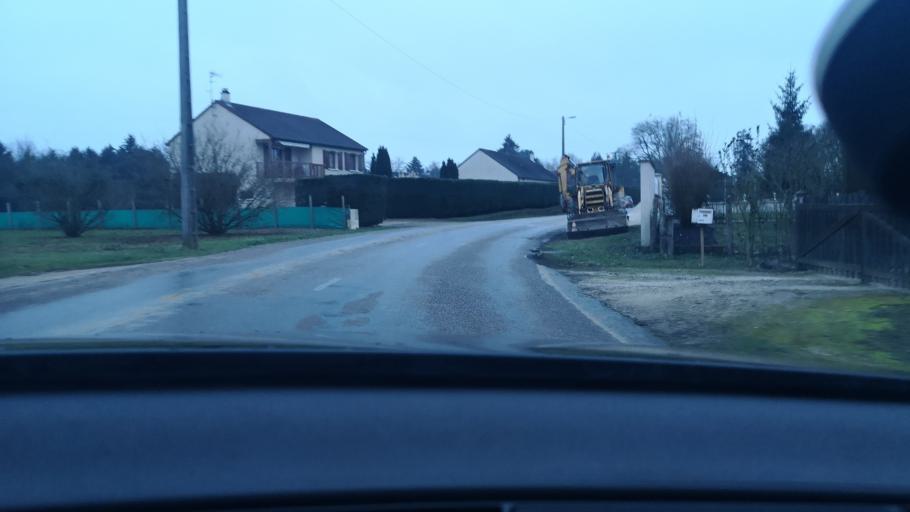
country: FR
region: Bourgogne
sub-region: Departement de la Cote-d'Or
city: Seurre
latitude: 47.0297
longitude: 5.0658
